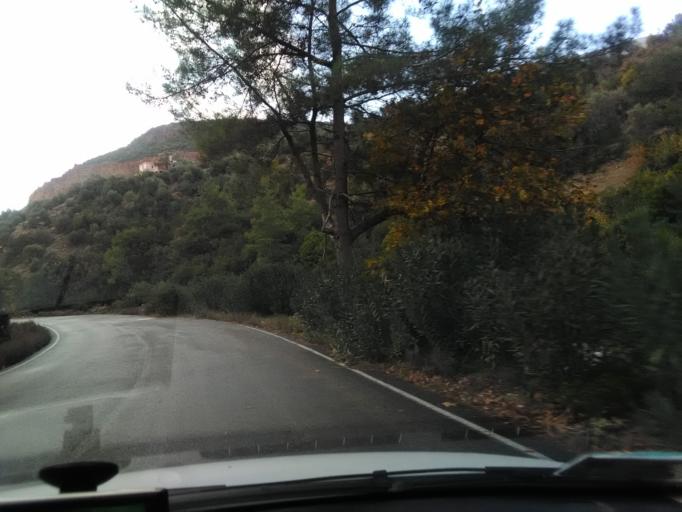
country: TR
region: Antalya
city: Gazipasa
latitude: 36.2847
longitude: 32.3678
